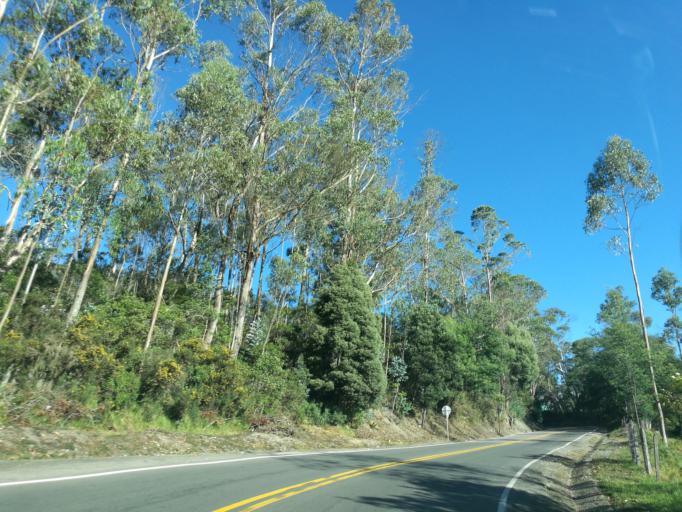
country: CO
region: Boyaca
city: Chiquinquira
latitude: 5.6199
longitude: -73.7785
